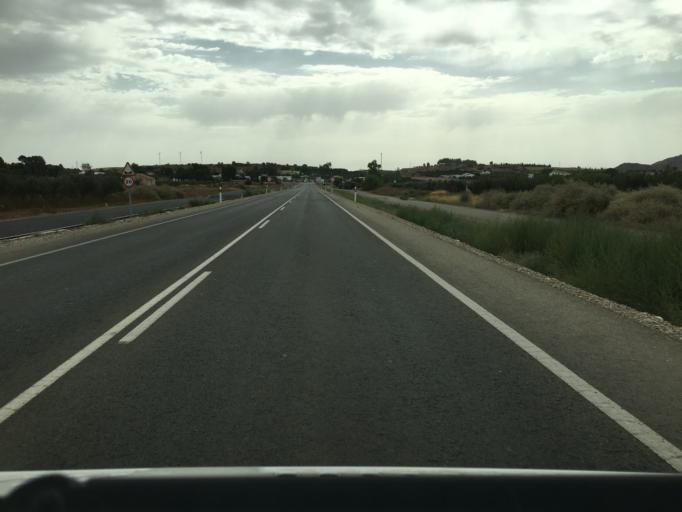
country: ES
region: Andalusia
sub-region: Provincia de Almeria
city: Huercal-Overa
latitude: 37.4172
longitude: -1.8840
